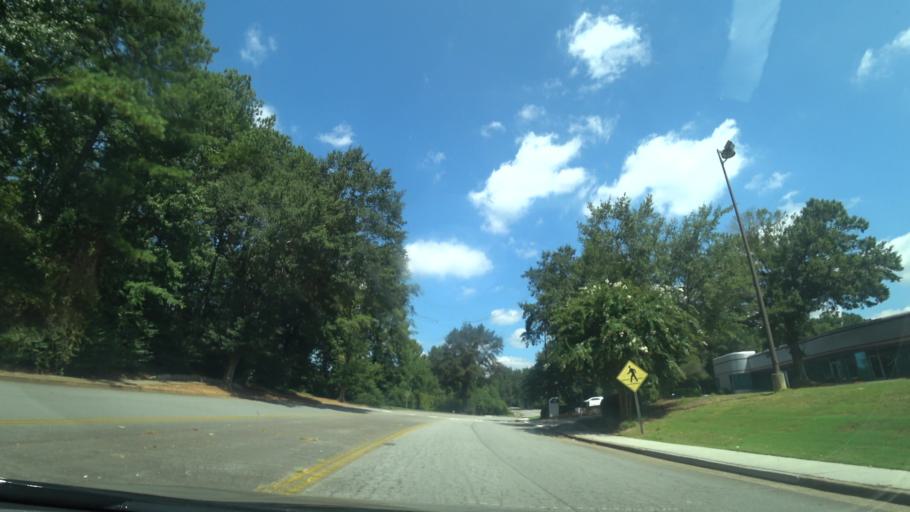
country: US
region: Georgia
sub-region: Gwinnett County
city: Norcross
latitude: 33.9285
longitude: -84.1839
